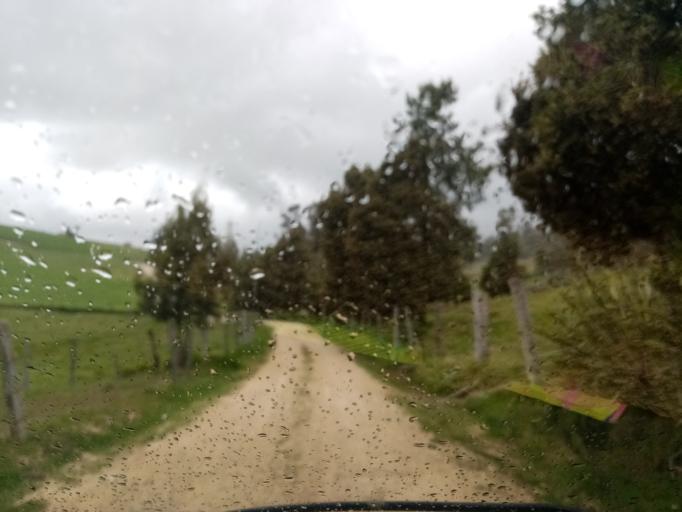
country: CO
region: Boyaca
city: Siachoque
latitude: 5.5559
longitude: -73.2510
